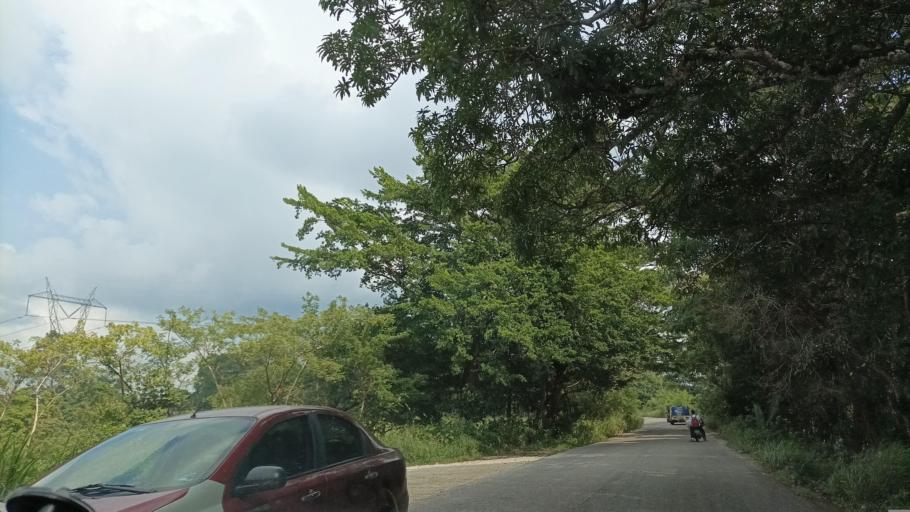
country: MX
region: Veracruz
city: Las Choapas
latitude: 17.7878
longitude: -94.1096
